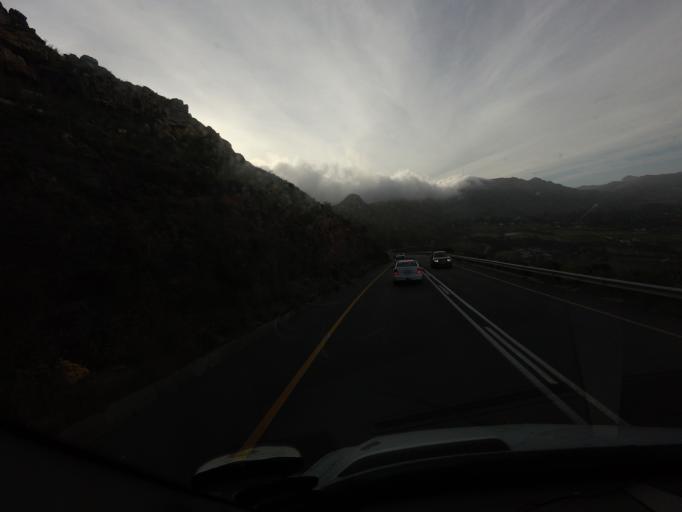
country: ZA
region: Western Cape
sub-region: City of Cape Town
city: Bergvliet
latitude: -34.0859
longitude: 18.4279
